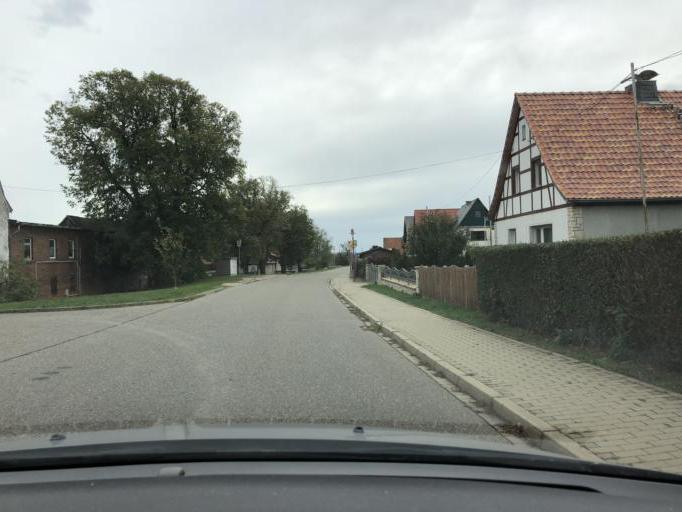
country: DE
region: Saxony-Anhalt
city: Bad Kosen
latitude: 51.1406
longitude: 11.7064
